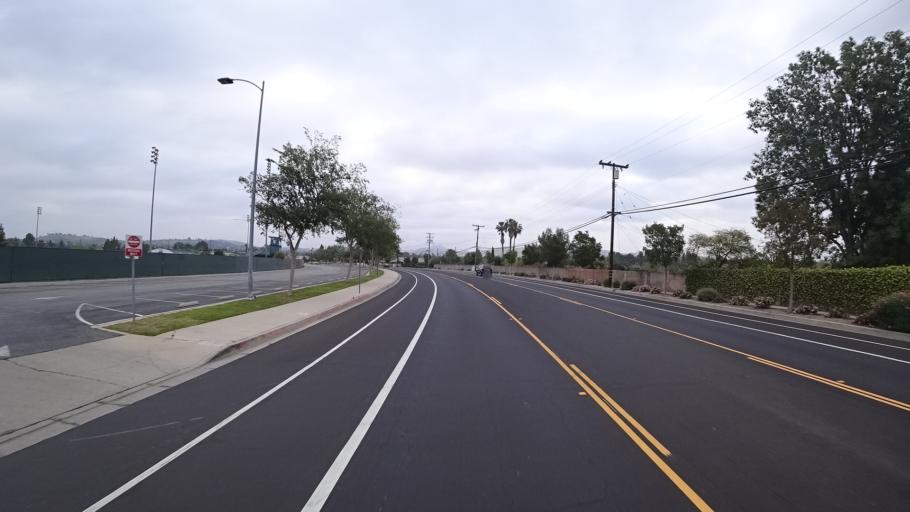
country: US
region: California
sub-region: Ventura County
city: Thousand Oaks
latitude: 34.2082
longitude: -118.8722
